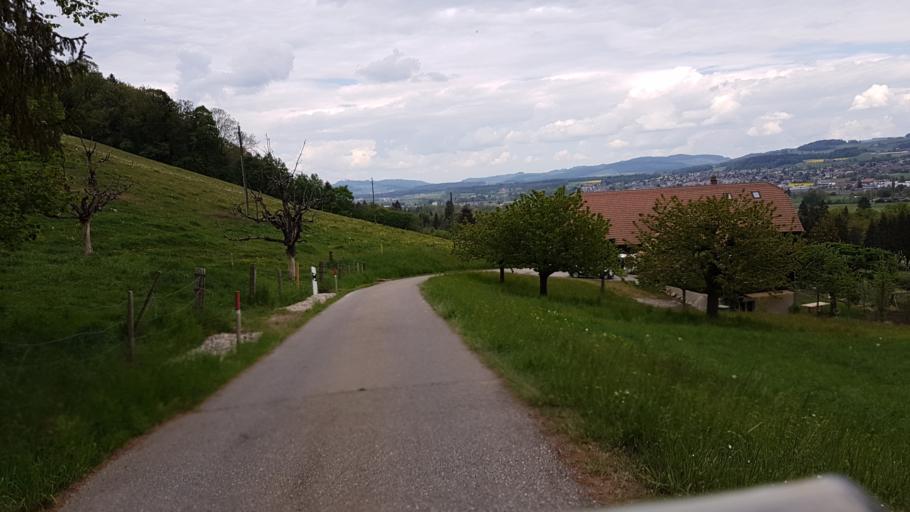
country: CH
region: Bern
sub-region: Bern-Mittelland District
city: Munsingen
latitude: 46.8522
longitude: 7.5518
